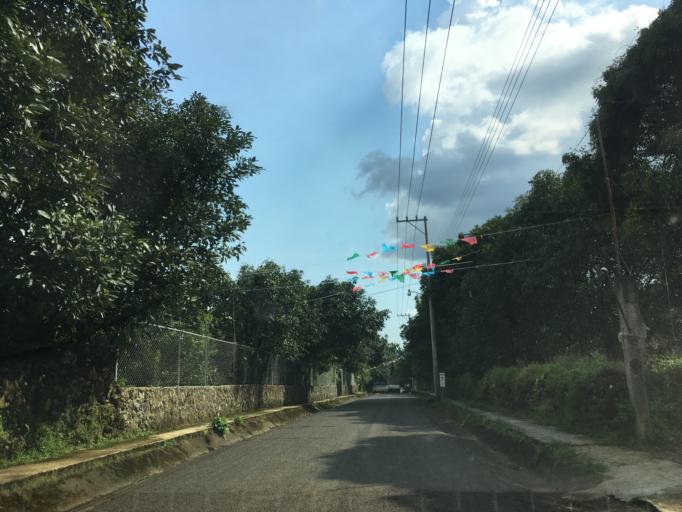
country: MX
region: Michoacan
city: Tingambato
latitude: 19.4499
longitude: -101.8676
